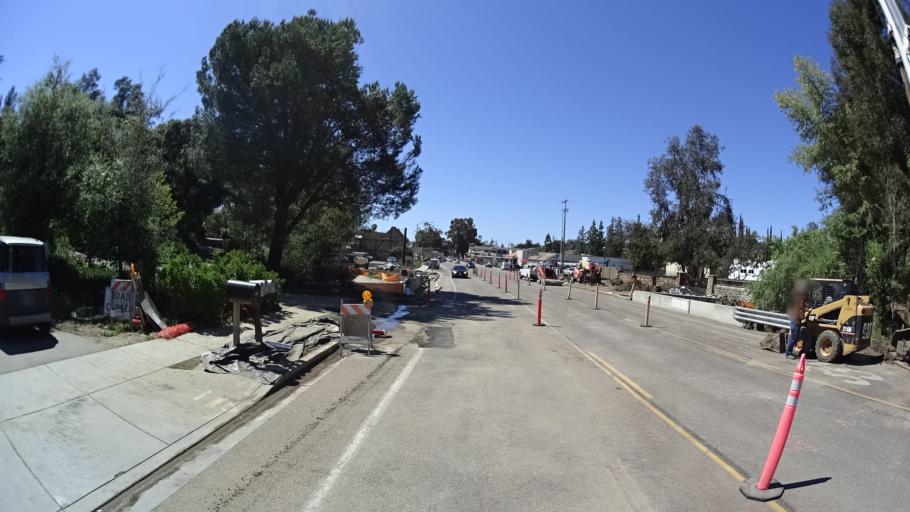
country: US
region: California
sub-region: San Diego County
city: Alpine
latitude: 32.8354
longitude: -116.7636
